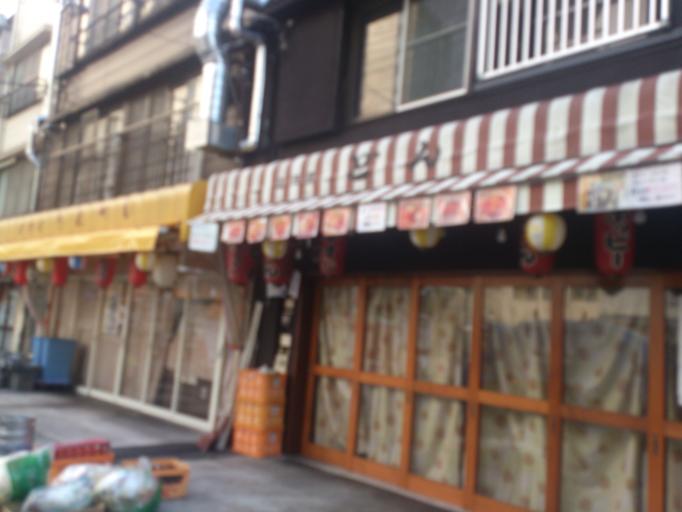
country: JP
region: Tokyo
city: Urayasu
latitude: 35.7134
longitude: 139.7943
